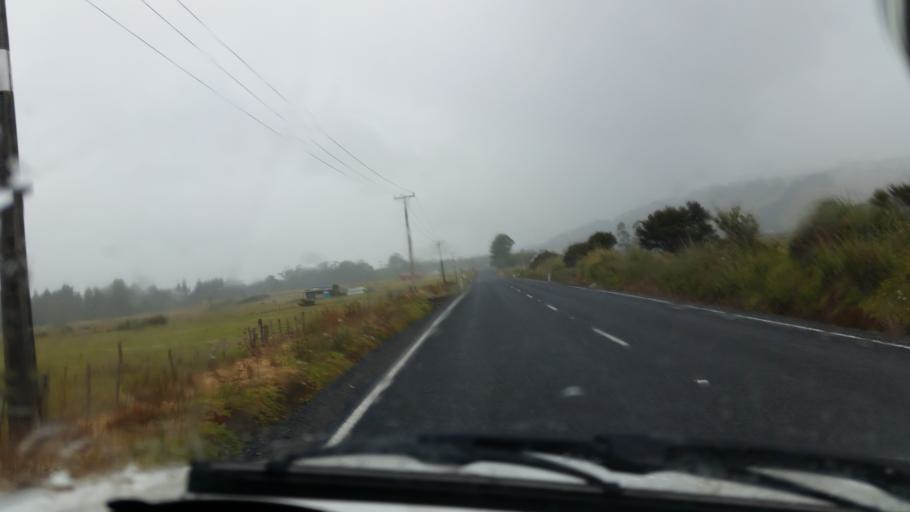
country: NZ
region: Northland
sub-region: Far North District
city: Ahipara
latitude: -35.1790
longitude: 173.1691
